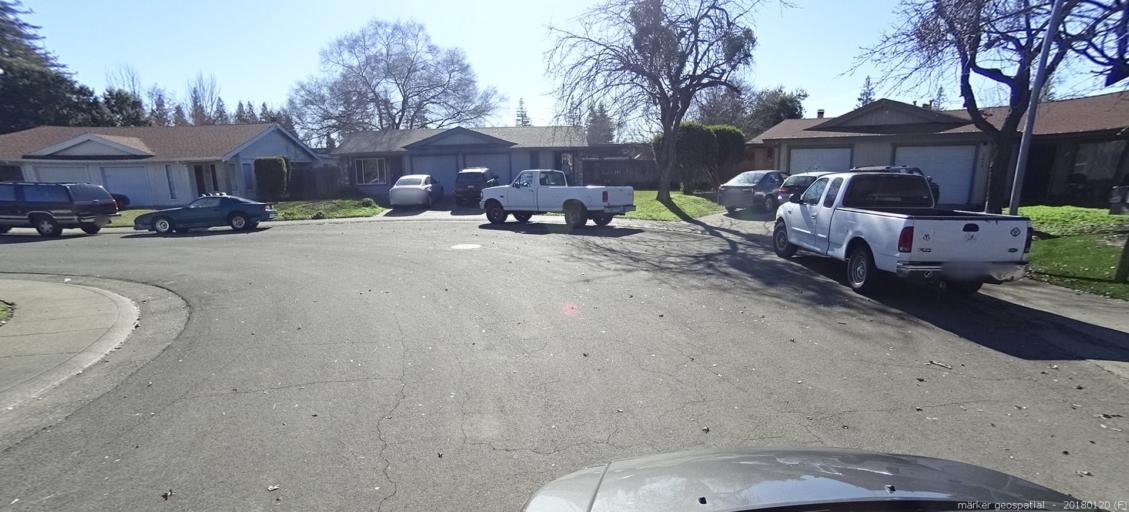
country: US
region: California
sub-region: Sacramento County
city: La Riviera
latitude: 38.5635
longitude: -121.3316
